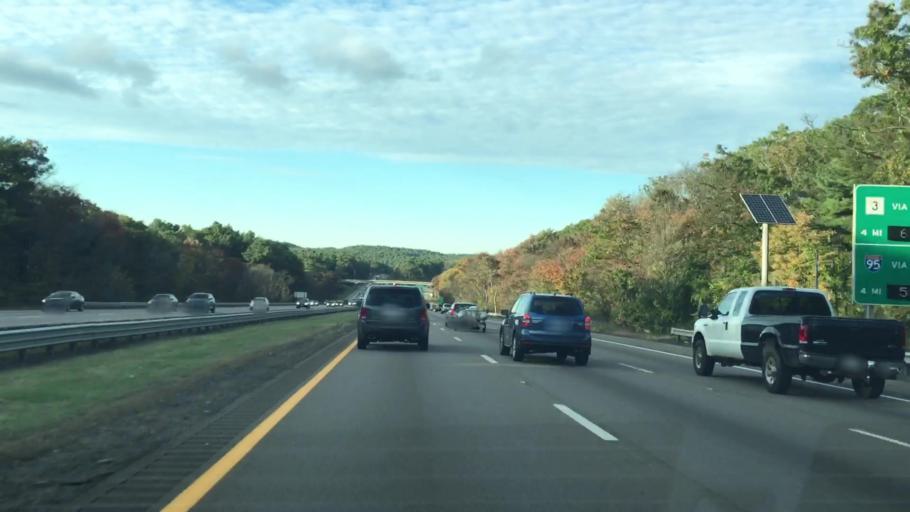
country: US
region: Massachusetts
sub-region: Norfolk County
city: Randolph
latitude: 42.1876
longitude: -71.0768
